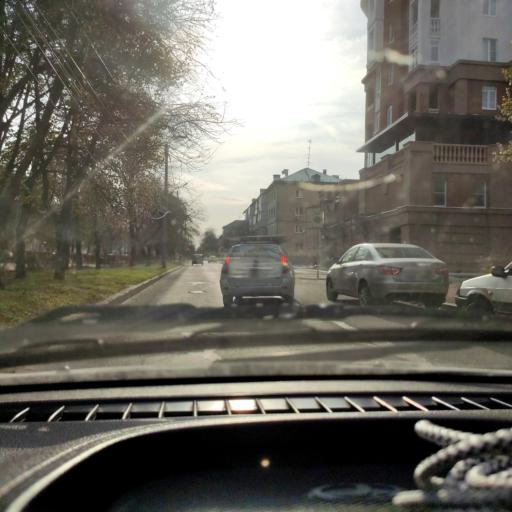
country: RU
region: Samara
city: Tol'yatti
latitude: 53.5092
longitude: 49.4114
